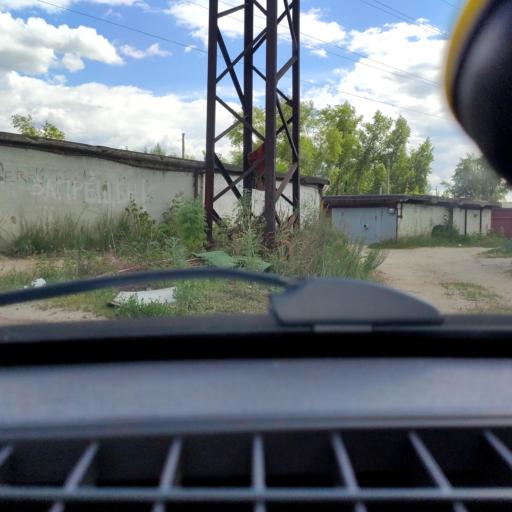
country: RU
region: Samara
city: Zhigulevsk
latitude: 53.4690
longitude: 49.5180
